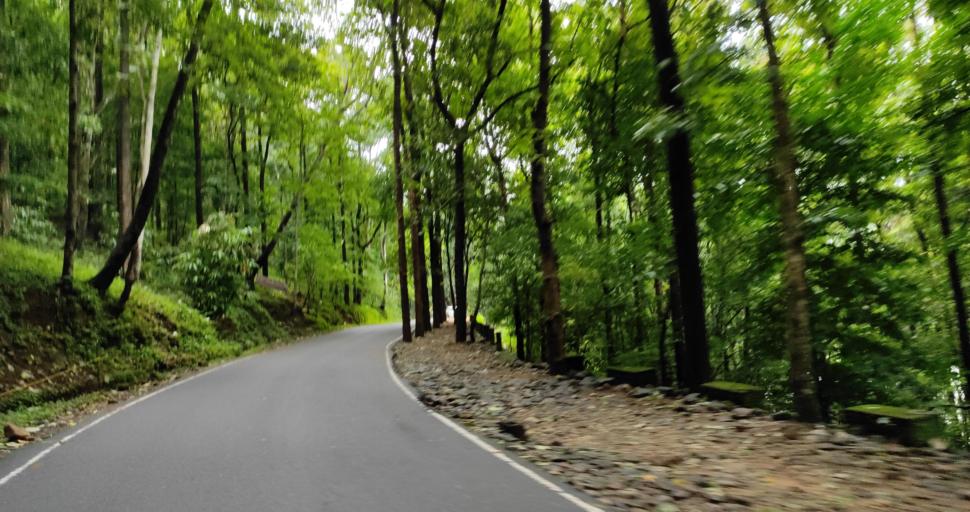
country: IN
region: Kerala
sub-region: Ernakulam
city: Angamali
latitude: 10.2910
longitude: 76.5664
